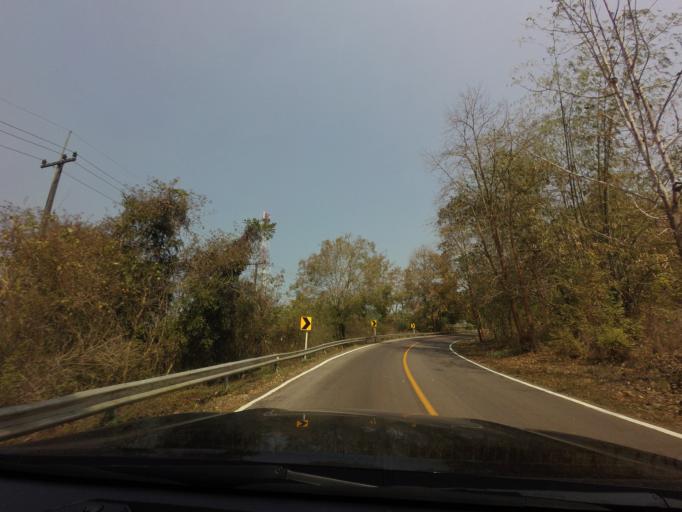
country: TH
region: Kanchanaburi
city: Thong Pha Phum
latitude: 14.7438
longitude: 98.5766
